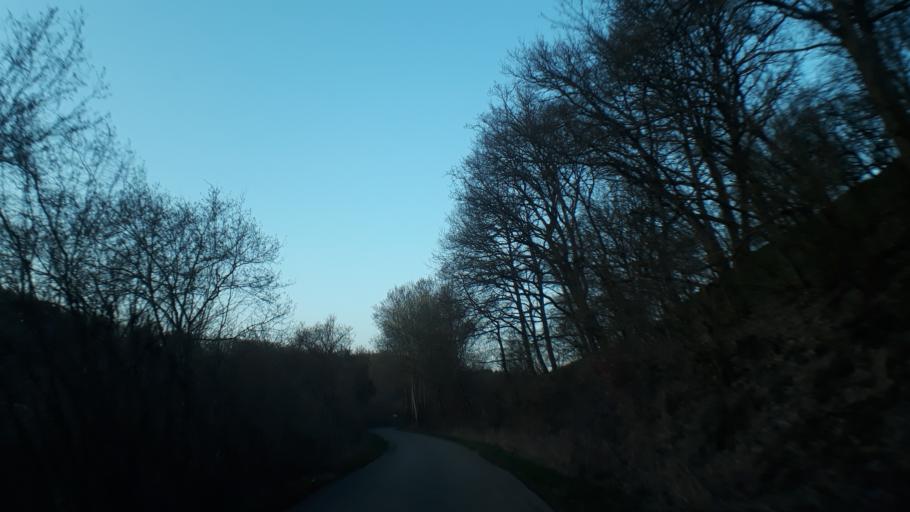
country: DE
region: Rheinland-Pfalz
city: Hummel
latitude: 50.5051
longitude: 6.7611
